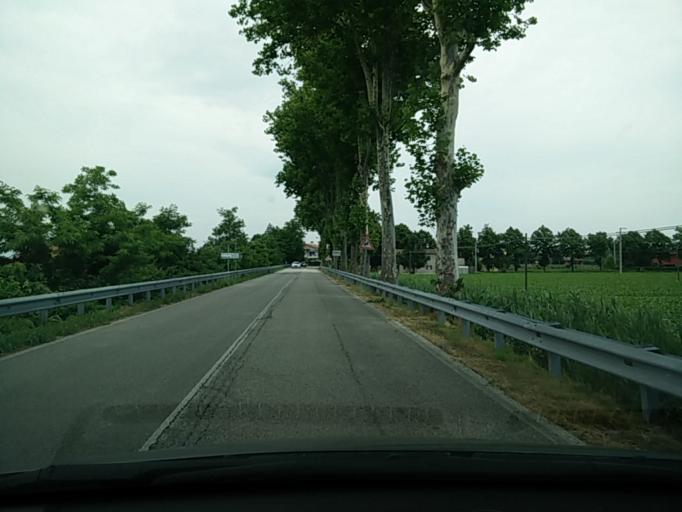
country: IT
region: Veneto
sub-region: Provincia di Venezia
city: Musile di Piave
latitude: 45.5859
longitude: 12.5473
